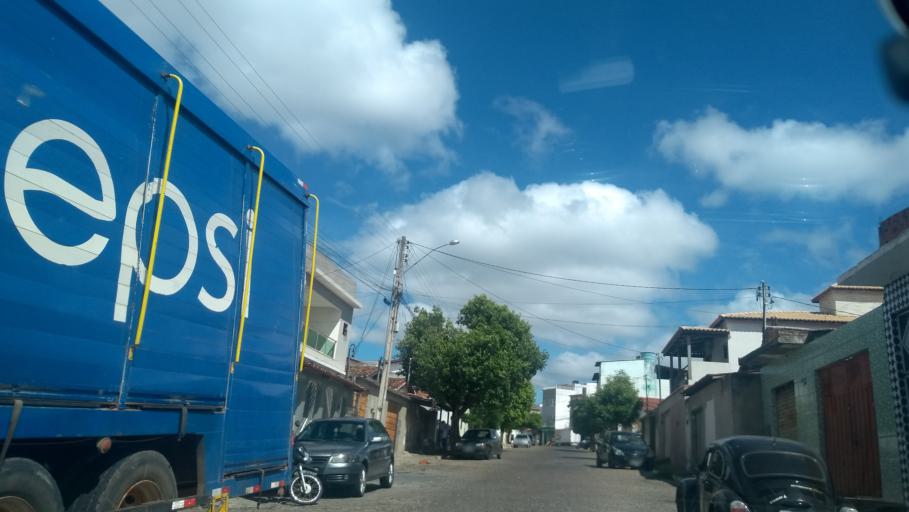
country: BR
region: Bahia
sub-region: Brumado
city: Brumado
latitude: -14.2111
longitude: -41.6755
